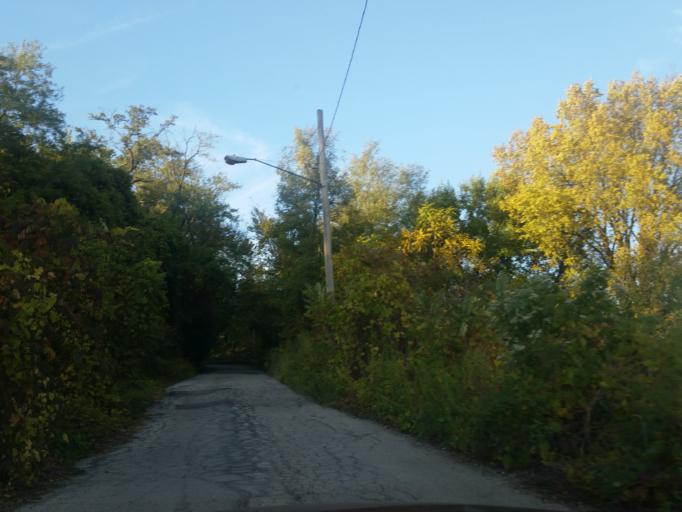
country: US
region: Ohio
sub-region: Cuyahoga County
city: Brooklyn Heights
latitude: 41.4490
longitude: -81.6892
